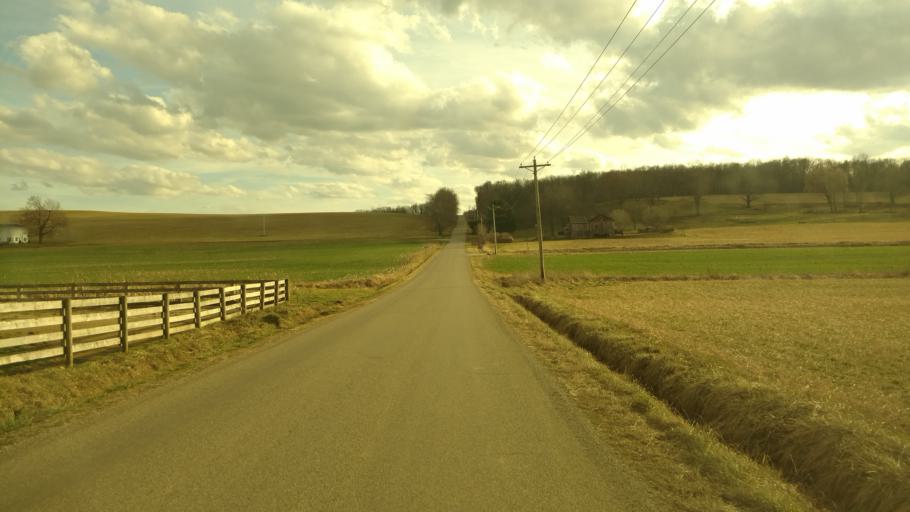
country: US
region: Ohio
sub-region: Knox County
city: Fredericktown
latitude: 40.5195
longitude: -82.4453
